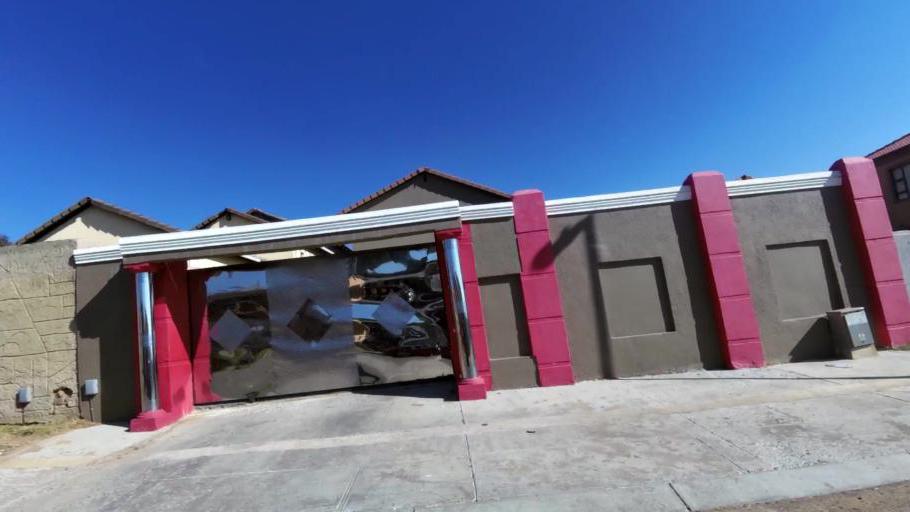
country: ZA
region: Gauteng
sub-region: City of Johannesburg Metropolitan Municipality
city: Johannesburg
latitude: -26.2551
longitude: 27.9866
